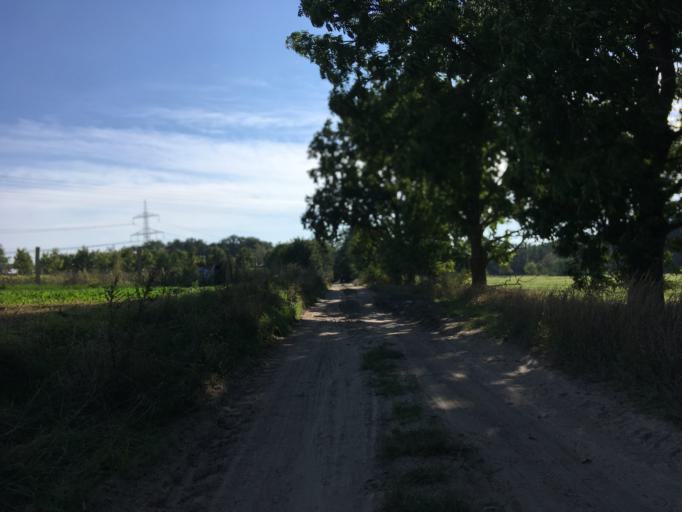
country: DE
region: Brandenburg
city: Altlandsberg
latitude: 52.5462
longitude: 13.7242
